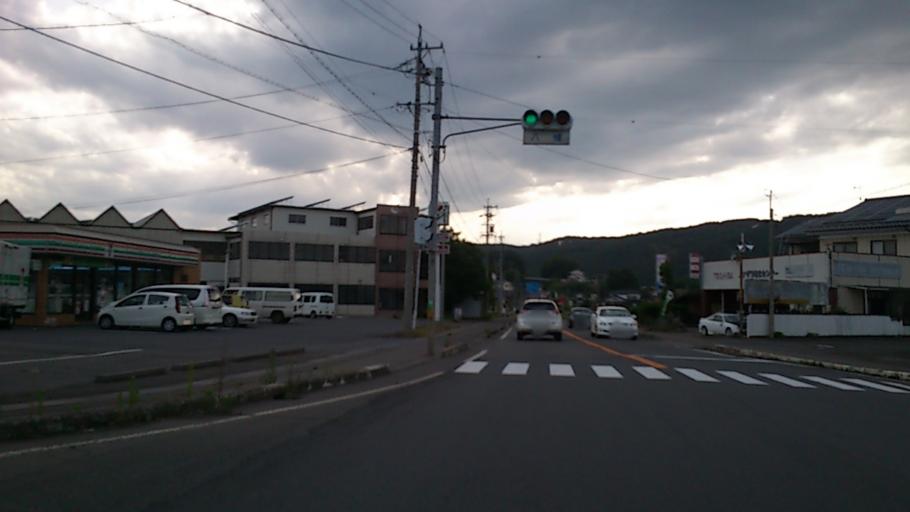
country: JP
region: Nagano
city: Komoro
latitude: 36.2688
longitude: 138.3959
